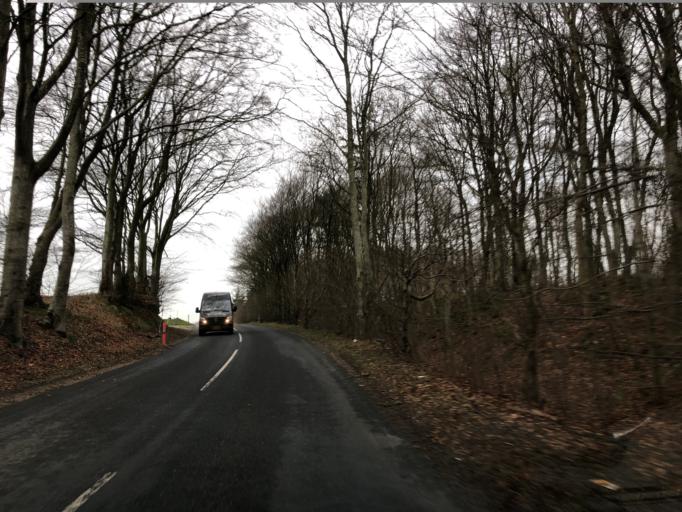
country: DK
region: Central Jutland
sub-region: Viborg Kommune
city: Stoholm
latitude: 56.4394
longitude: 9.1069
